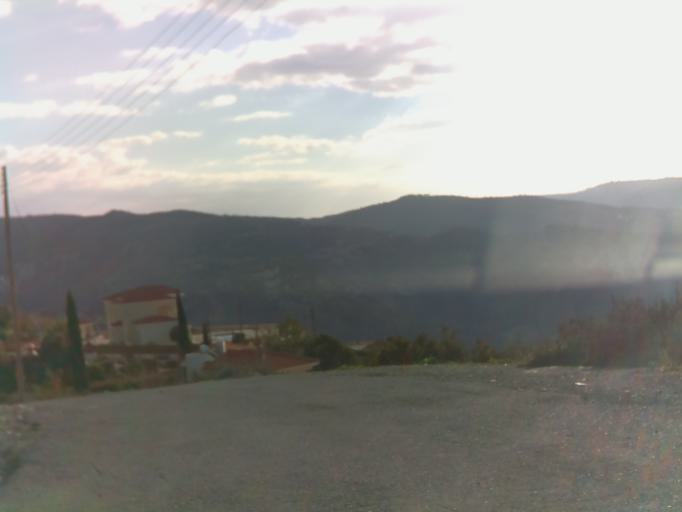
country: CY
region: Pafos
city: Pegeia
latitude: 34.8961
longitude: 32.3844
